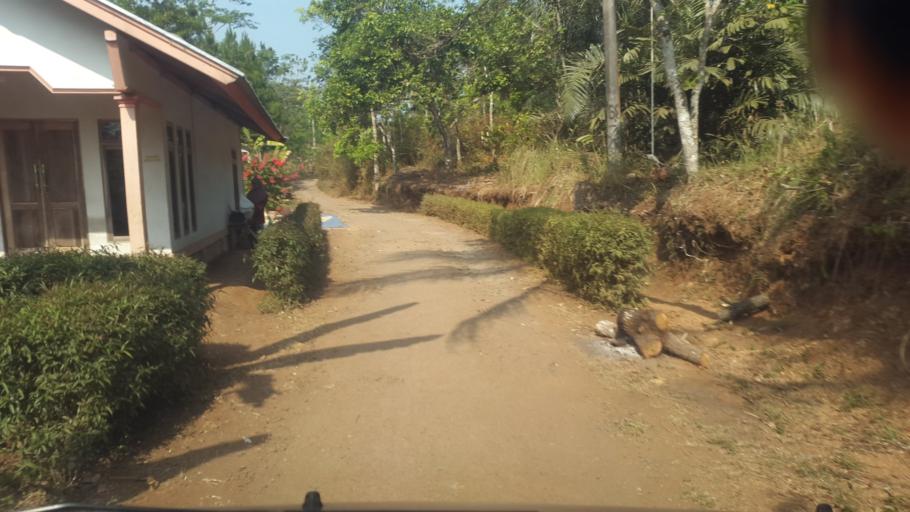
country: ID
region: West Java
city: Ciroyom
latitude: -7.1158
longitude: 106.8237
